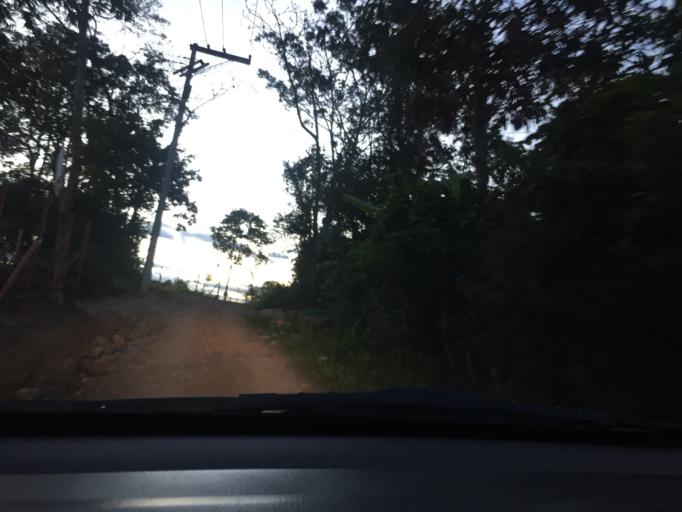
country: CO
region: Cundinamarca
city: Zipacon
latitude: 4.7166
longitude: -74.4135
